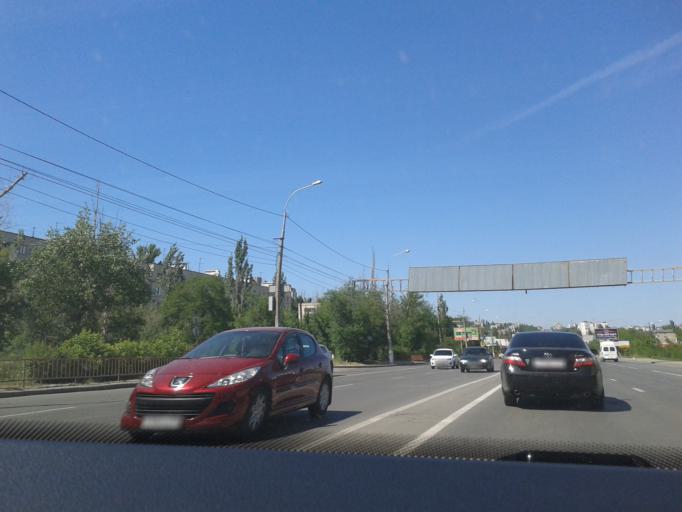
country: RU
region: Volgograd
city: Volgograd
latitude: 48.6508
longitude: 44.4353
